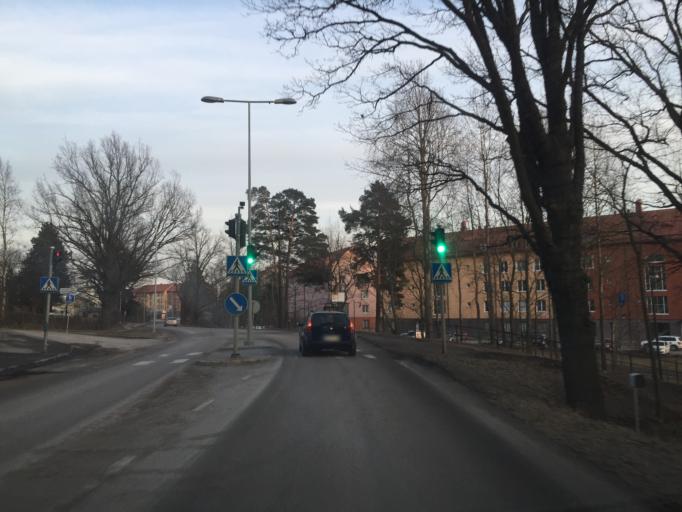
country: FI
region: Uusimaa
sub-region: Helsinki
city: Vantaa
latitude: 60.2854
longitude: 24.9618
